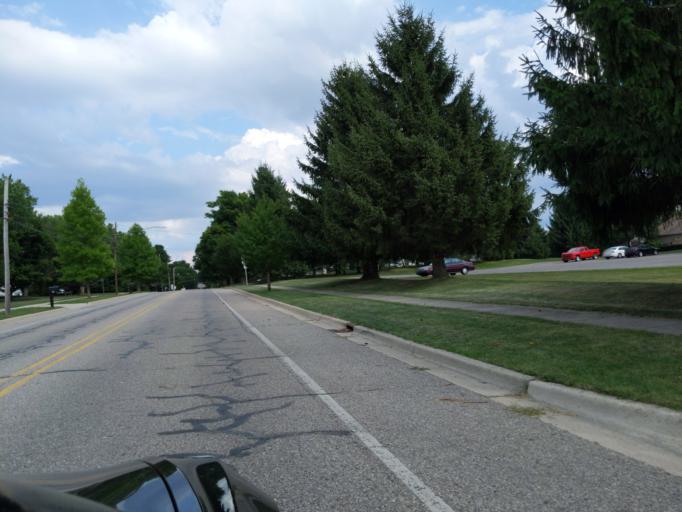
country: US
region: Michigan
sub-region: Clinton County
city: DeWitt
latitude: 42.8358
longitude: -84.5611
